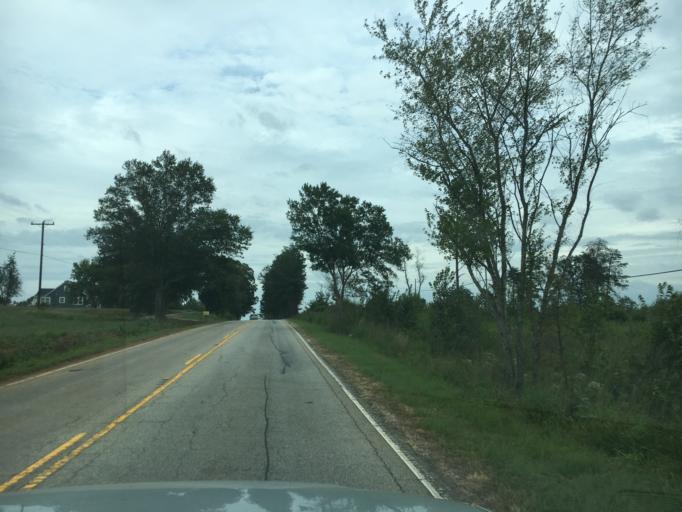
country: US
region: South Carolina
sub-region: Spartanburg County
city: Duncan
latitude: 34.9368
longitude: -82.1748
